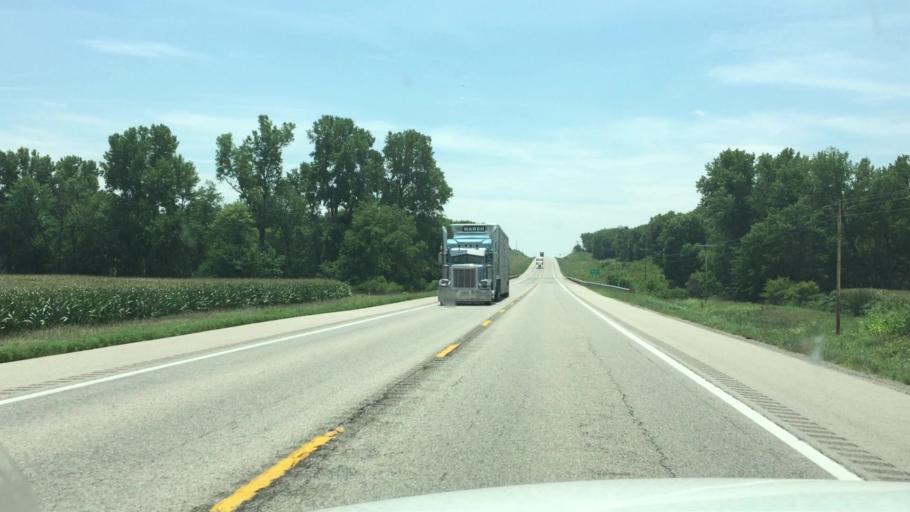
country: US
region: Kansas
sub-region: Jackson County
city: Holton
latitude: 39.6308
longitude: -95.7311
